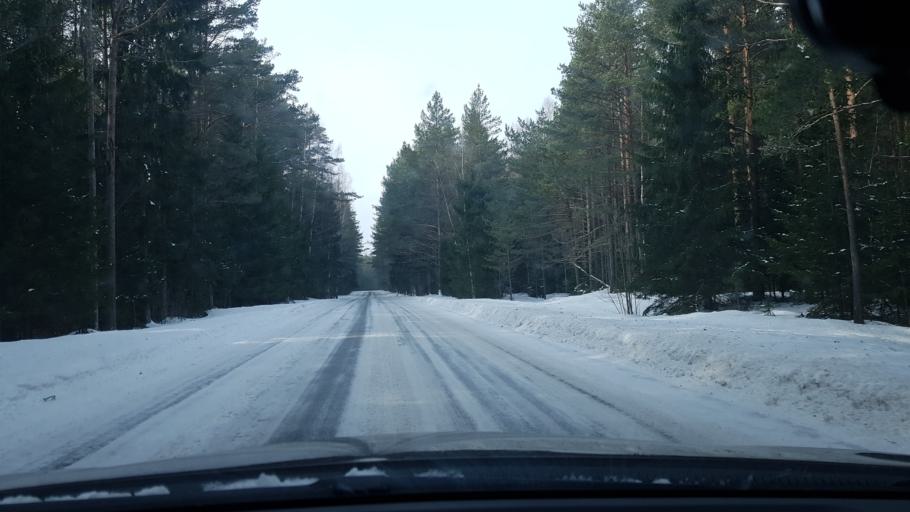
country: EE
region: Harju
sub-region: Kuusalu vald
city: Kuusalu
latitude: 59.5566
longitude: 25.5561
